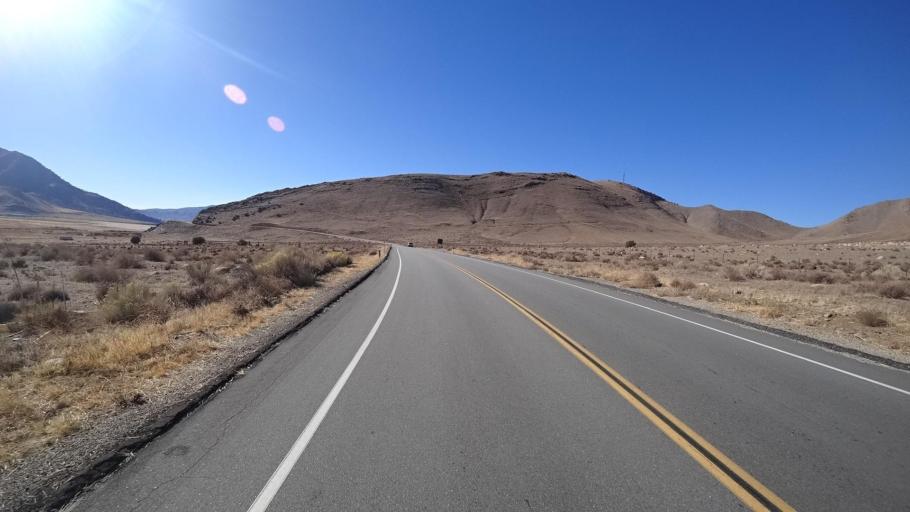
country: US
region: California
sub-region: Kern County
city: Wofford Heights
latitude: 35.6806
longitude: -118.4082
